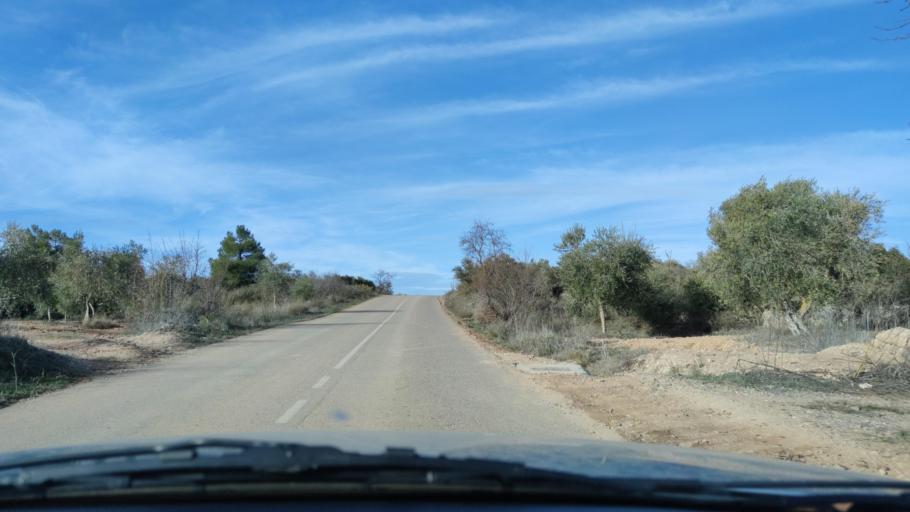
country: ES
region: Catalonia
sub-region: Provincia de Lleida
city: el Cogul
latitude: 41.4667
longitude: 0.6740
